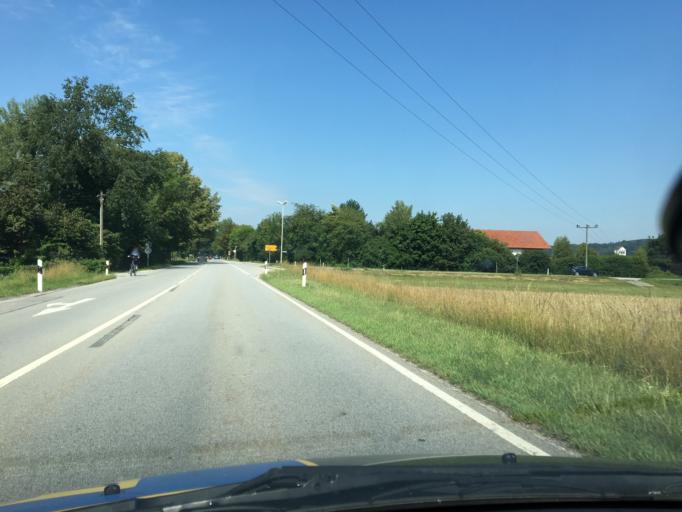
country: DE
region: Bavaria
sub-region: Upper Bavaria
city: Aresing
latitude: 48.2705
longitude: 12.6075
